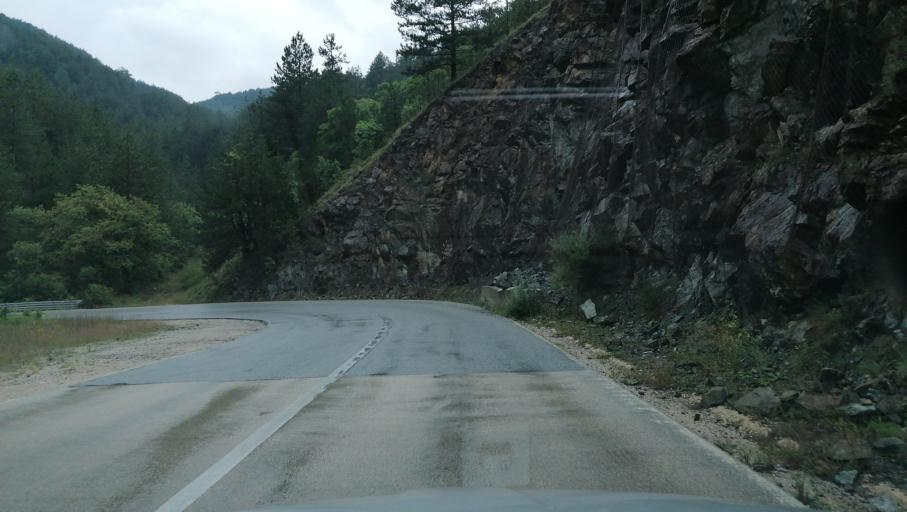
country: RS
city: Durici
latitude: 43.8202
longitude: 19.5069
